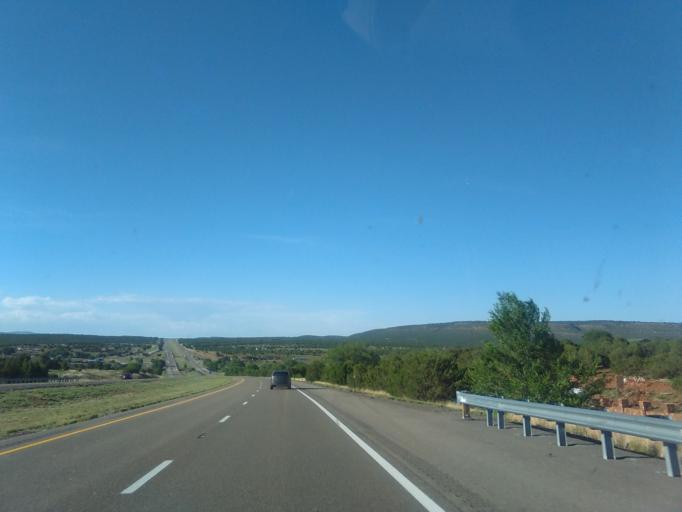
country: US
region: New Mexico
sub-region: San Miguel County
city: Las Vegas
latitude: 35.4507
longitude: -105.2791
